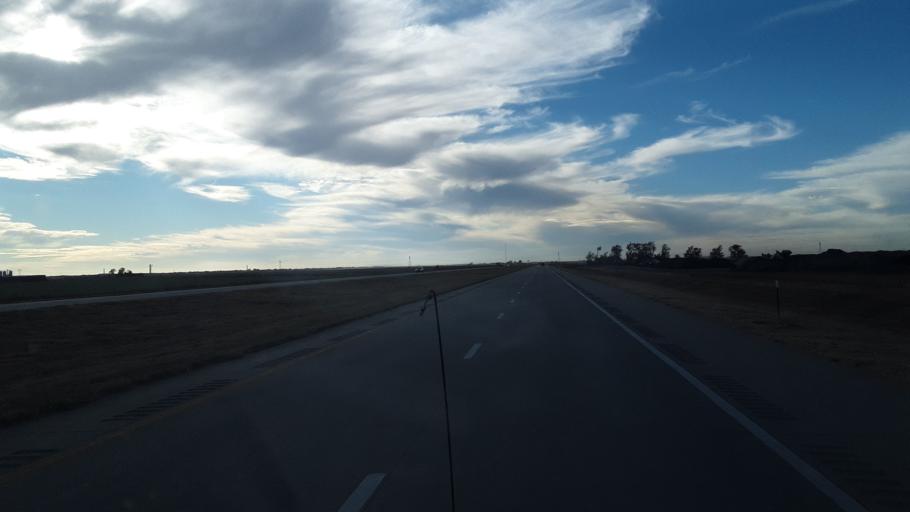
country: US
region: Kansas
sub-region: Finney County
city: Holcomb
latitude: 38.0034
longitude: -100.9419
